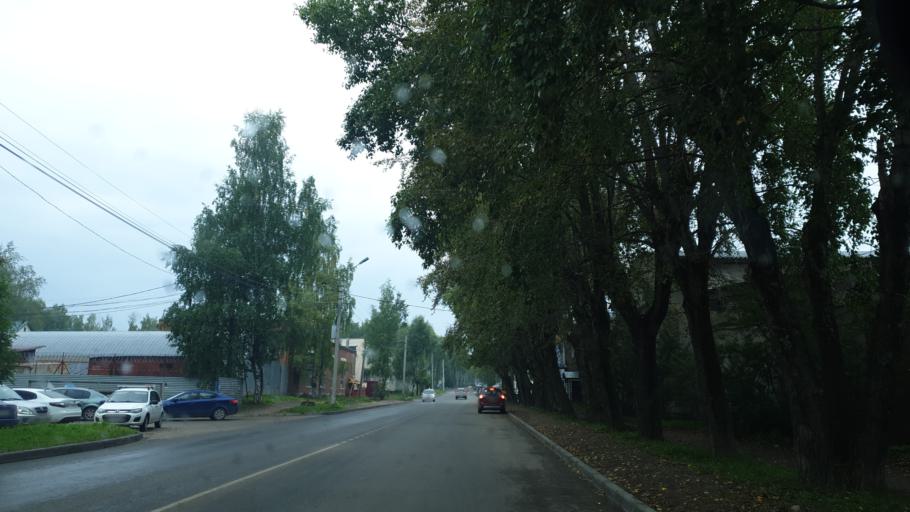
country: RU
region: Komi Republic
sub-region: Syktyvdinskiy Rayon
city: Syktyvkar
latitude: 61.6555
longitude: 50.8305
